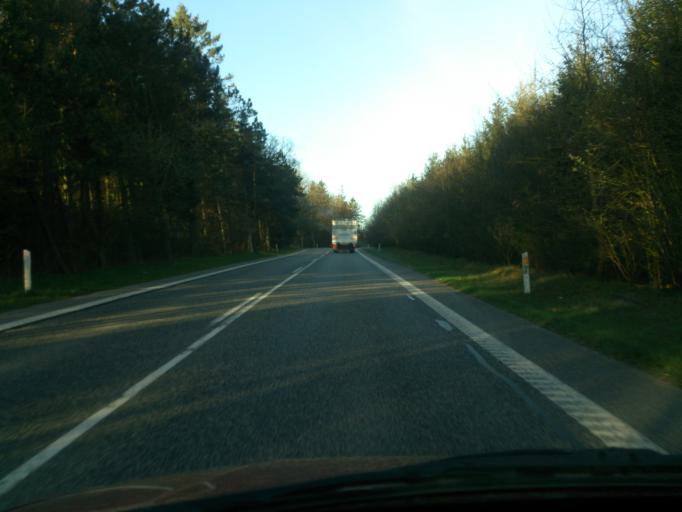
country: DK
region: Central Jutland
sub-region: Viborg Kommune
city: Bjerringbro
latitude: 56.4437
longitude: 9.7095
